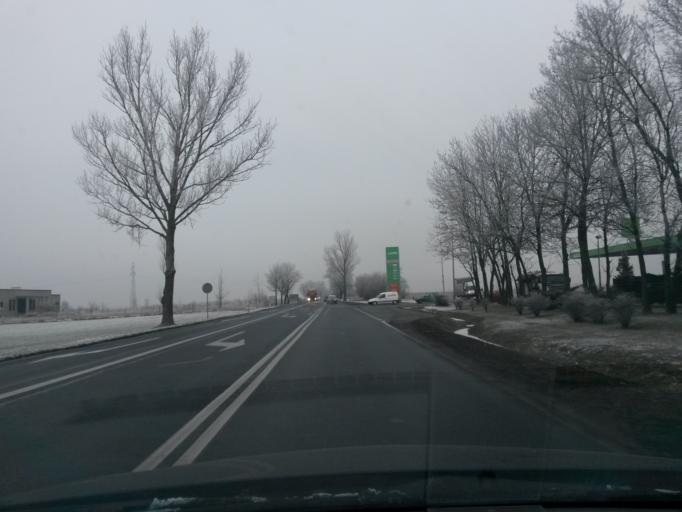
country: PL
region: Kujawsko-Pomorskie
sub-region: Powiat mogilenski
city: Strzelno
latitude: 52.6413
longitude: 18.1812
